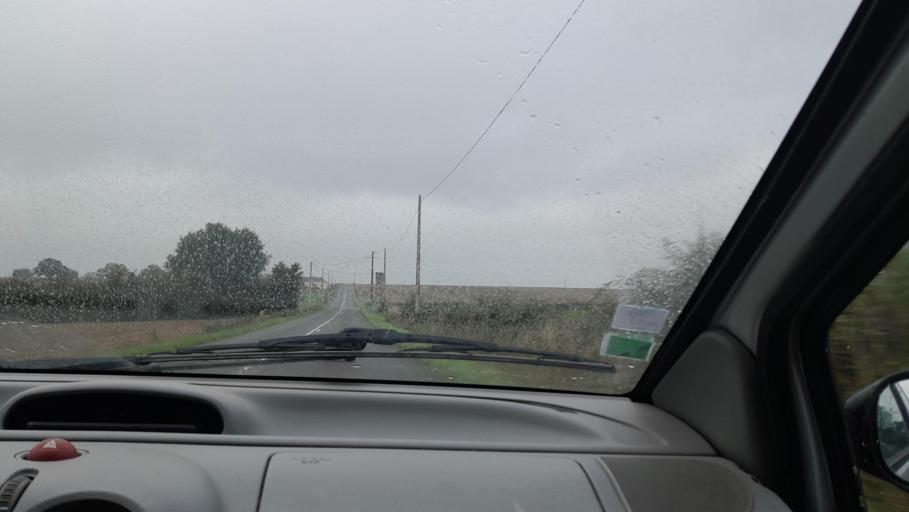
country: FR
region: Pays de la Loire
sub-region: Departement de la Mayenne
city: Congrier
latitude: 47.8516
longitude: -1.1351
